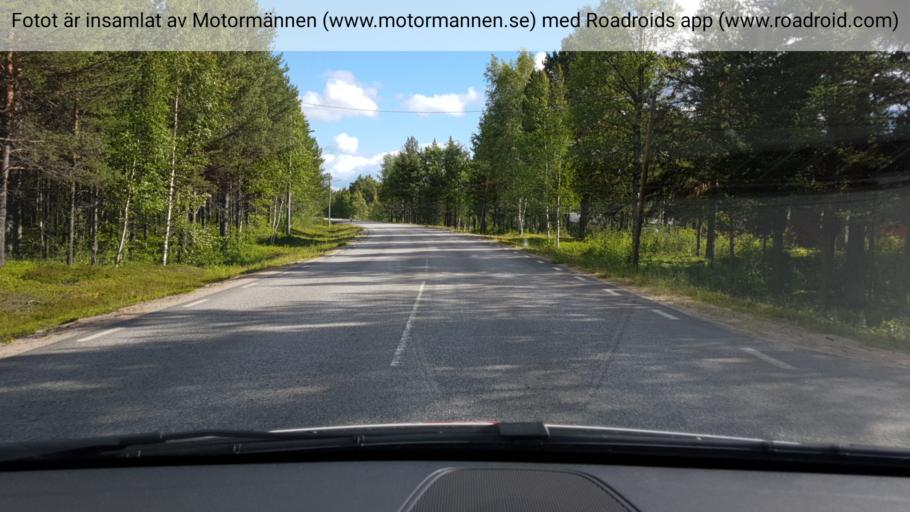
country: SE
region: Jaemtland
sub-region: Harjedalens Kommun
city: Sveg
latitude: 62.0396
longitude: 14.6387
